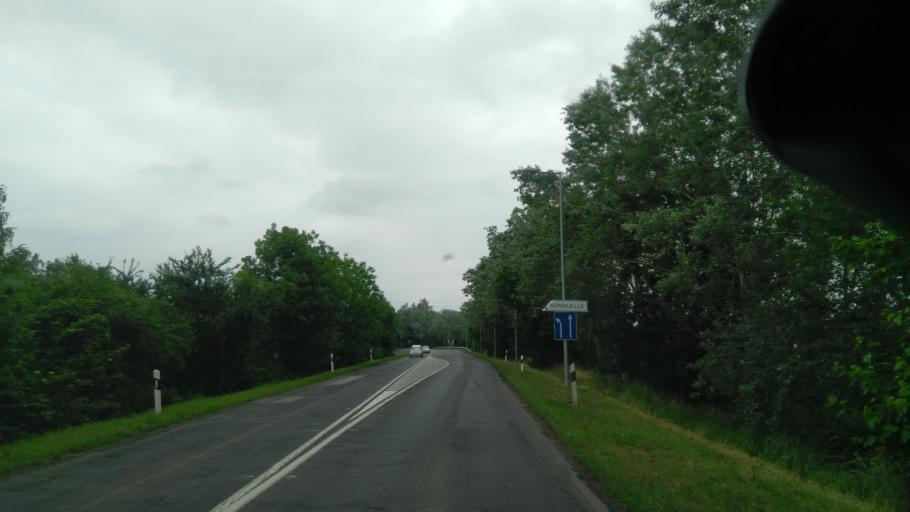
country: HU
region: Bekes
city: Bekescsaba
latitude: 46.6931
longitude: 21.0981
